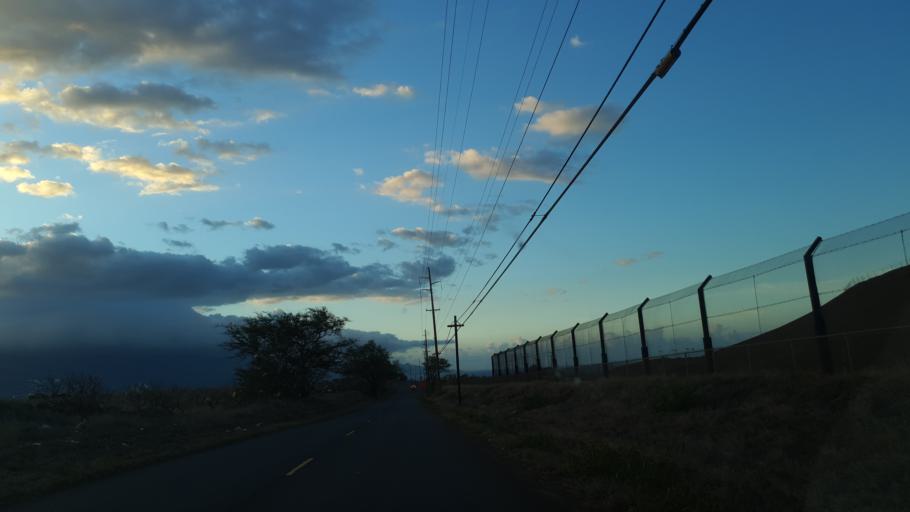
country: US
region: Hawaii
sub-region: Maui County
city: Kahului
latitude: 20.8557
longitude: -156.4222
